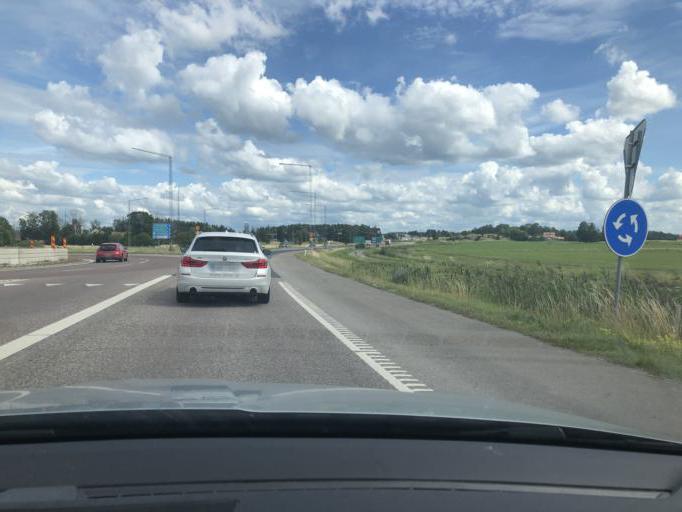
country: SE
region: Uppsala
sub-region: Uppsala Kommun
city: Saevja
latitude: 59.8437
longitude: 17.7008
